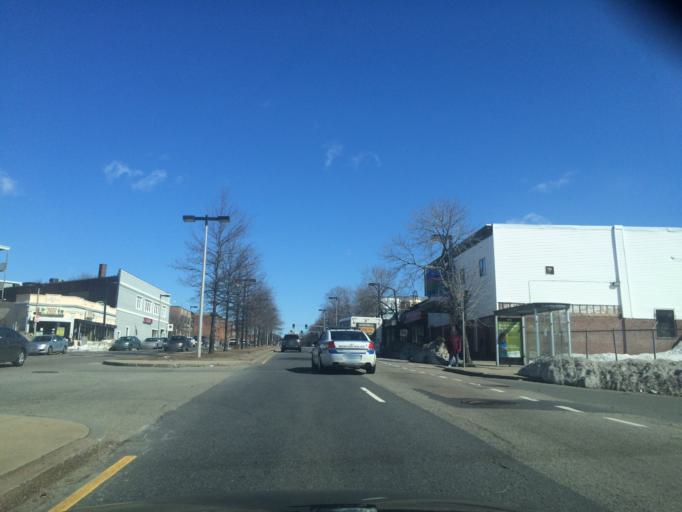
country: US
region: Massachusetts
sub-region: Suffolk County
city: Jamaica Plain
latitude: 42.2893
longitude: -71.0898
